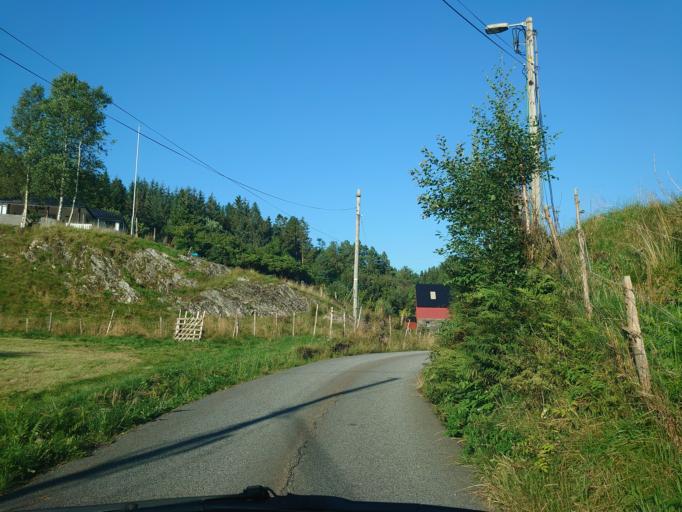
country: NO
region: Hordaland
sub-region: Bergen
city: Espeland
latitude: 60.3584
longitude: 5.4384
